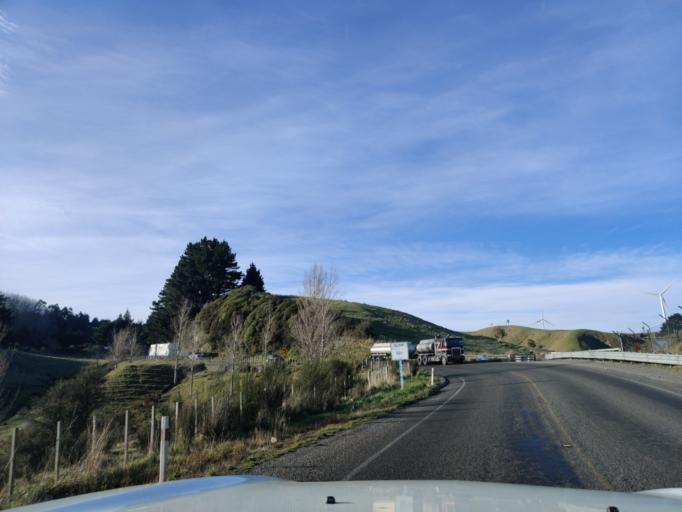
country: NZ
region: Manawatu-Wanganui
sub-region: Palmerston North City
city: Palmerston North
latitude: -40.2875
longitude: 175.7840
